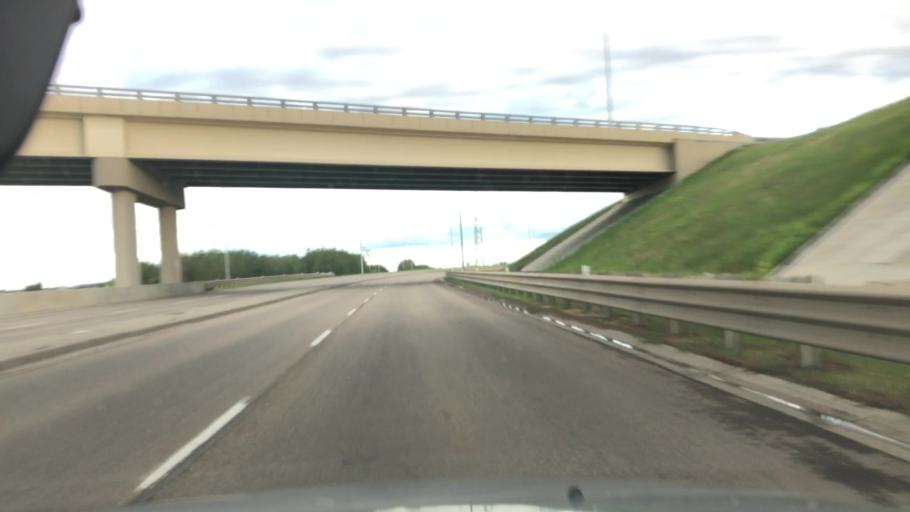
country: CA
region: Alberta
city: St. Albert
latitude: 53.6329
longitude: -113.5659
